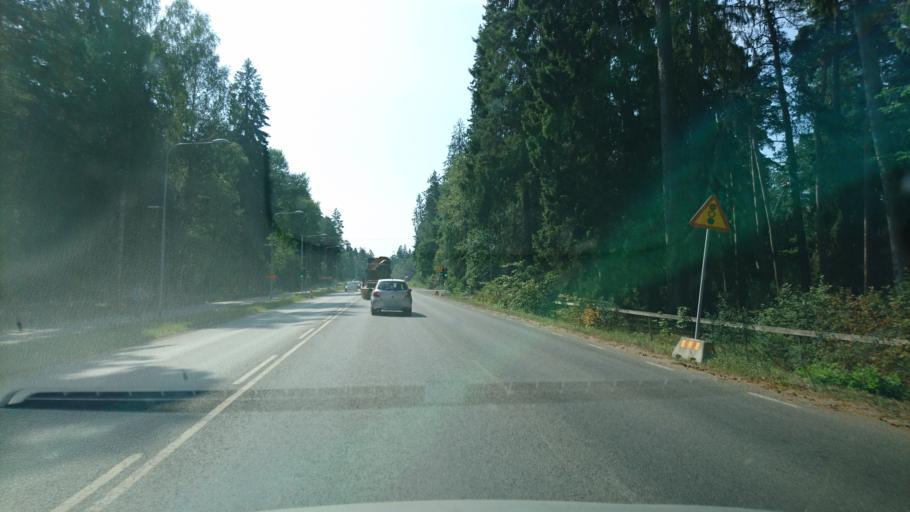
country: SE
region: Uppsala
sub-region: Uppsala Kommun
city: Uppsala
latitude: 59.8367
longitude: 17.6411
